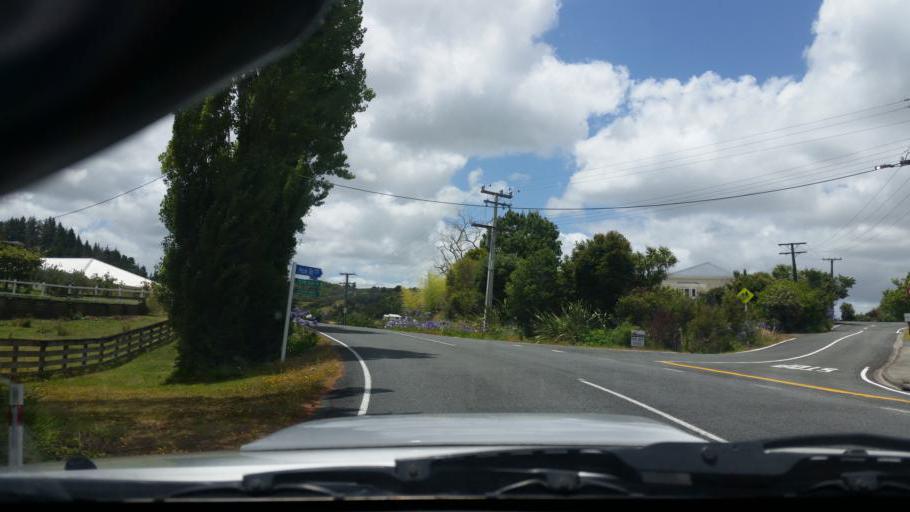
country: NZ
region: Northland
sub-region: Whangarei
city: Ruakaka
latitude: -36.0970
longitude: 174.2411
